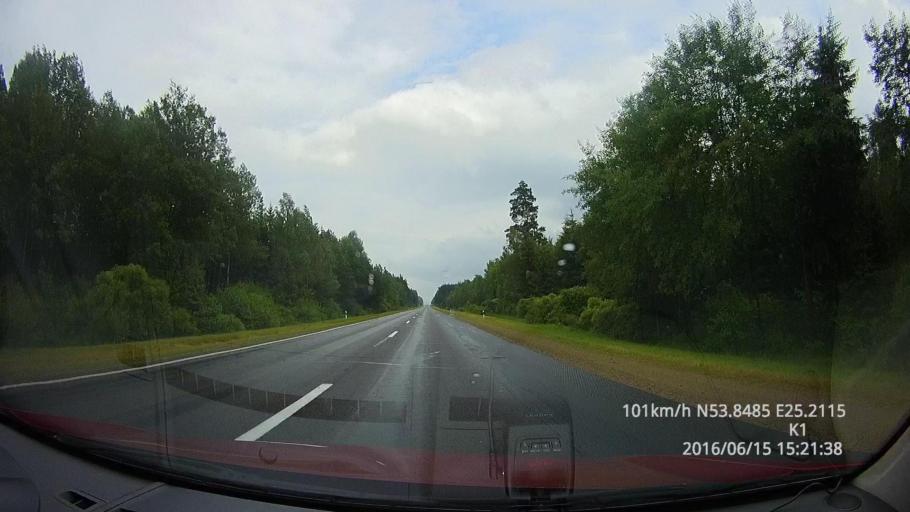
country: BY
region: Grodnenskaya
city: Lida
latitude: 53.8483
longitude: 25.2129
